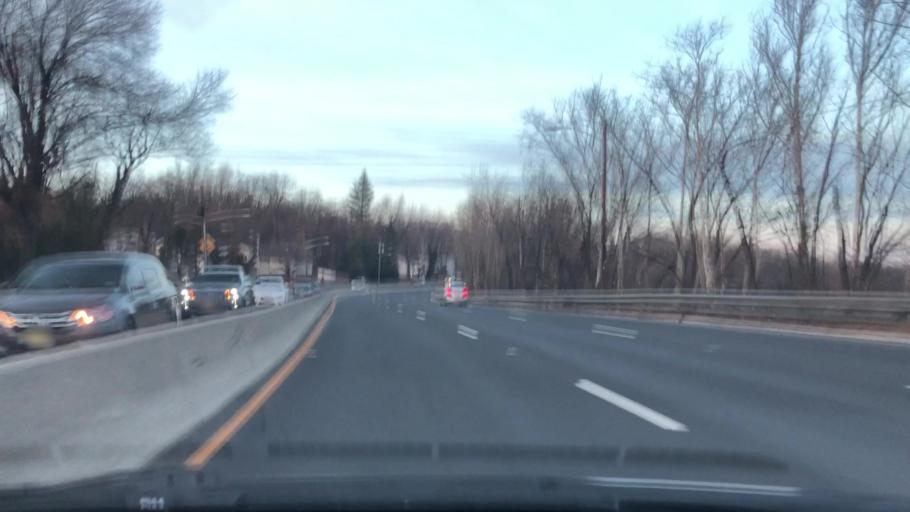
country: US
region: New Jersey
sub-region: Bergen County
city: Elmwood Park
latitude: 40.9113
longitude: -74.1340
